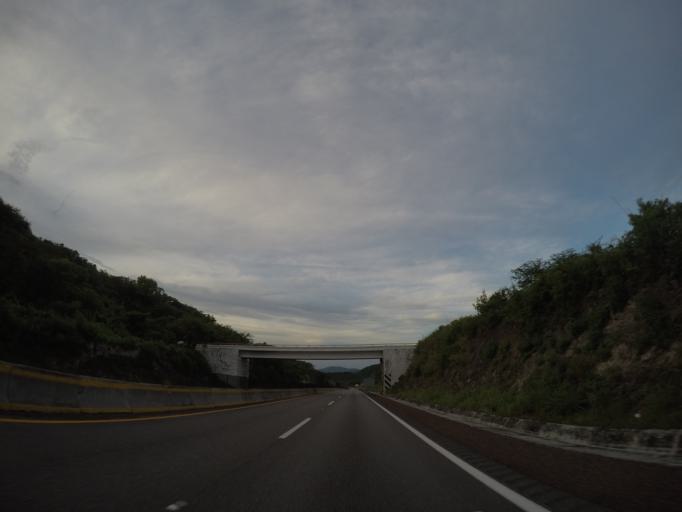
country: MX
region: Guerrero
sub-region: Huitzuco de los Figueroa
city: Ciudad de Huitzuco
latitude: 18.2987
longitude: -99.2028
